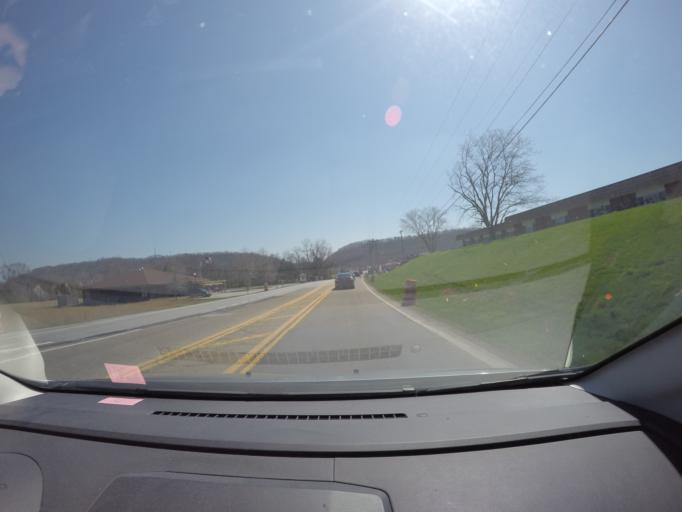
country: US
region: Tennessee
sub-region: Hamilton County
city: Collegedale
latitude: 35.0627
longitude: -85.0736
